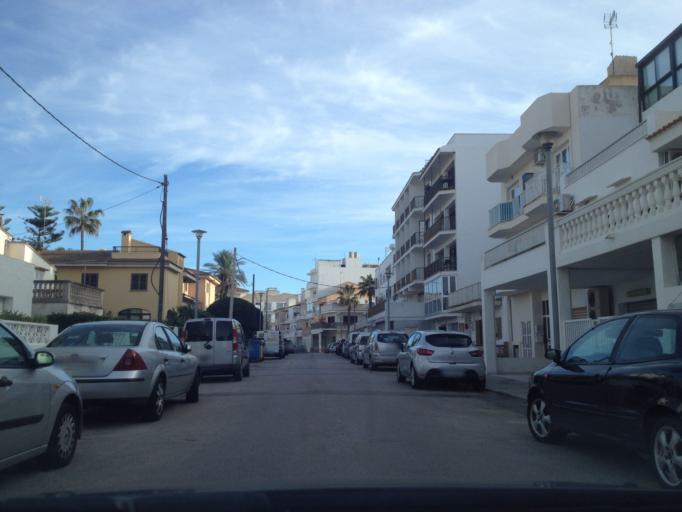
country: ES
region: Balearic Islands
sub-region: Illes Balears
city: Port d'Alcudia
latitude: 39.7687
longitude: 3.1500
